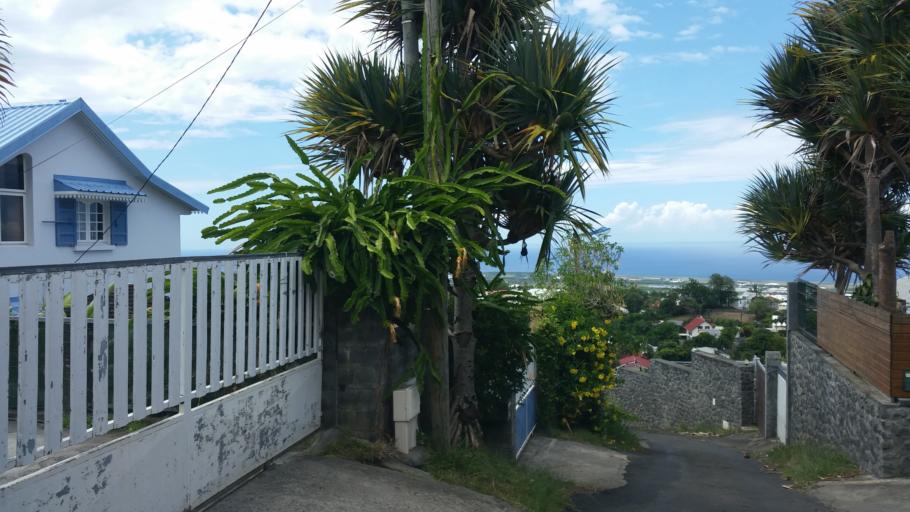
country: RE
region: Reunion
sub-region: Reunion
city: Sainte-Marie
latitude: -20.9310
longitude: 55.5232
